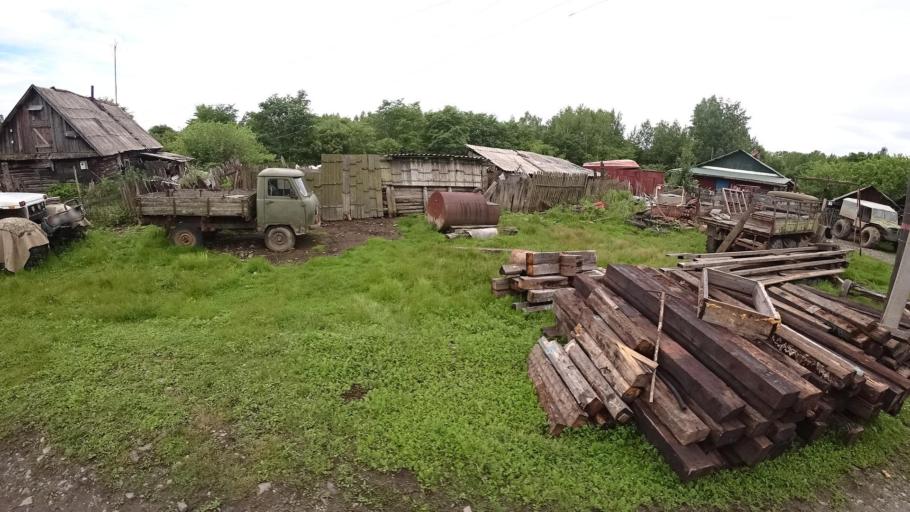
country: RU
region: Khabarovsk Krai
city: Amursk
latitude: 49.9067
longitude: 136.1327
